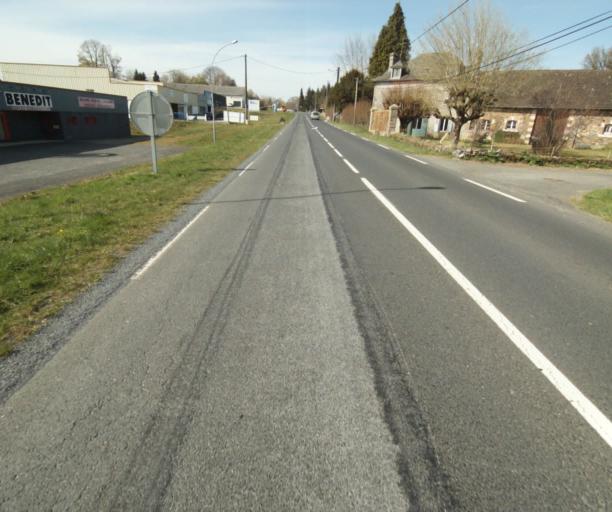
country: FR
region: Limousin
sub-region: Departement de la Correze
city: Naves
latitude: 45.3420
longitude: 1.7471
